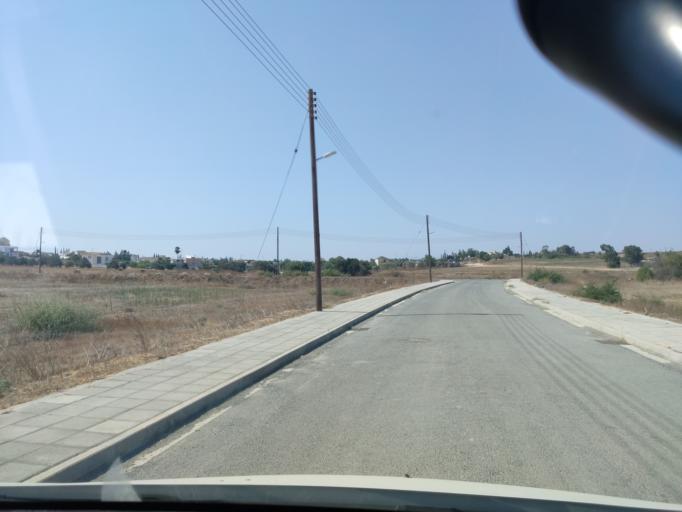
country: CY
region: Lefkosia
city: Geri
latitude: 35.1166
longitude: 33.4158
